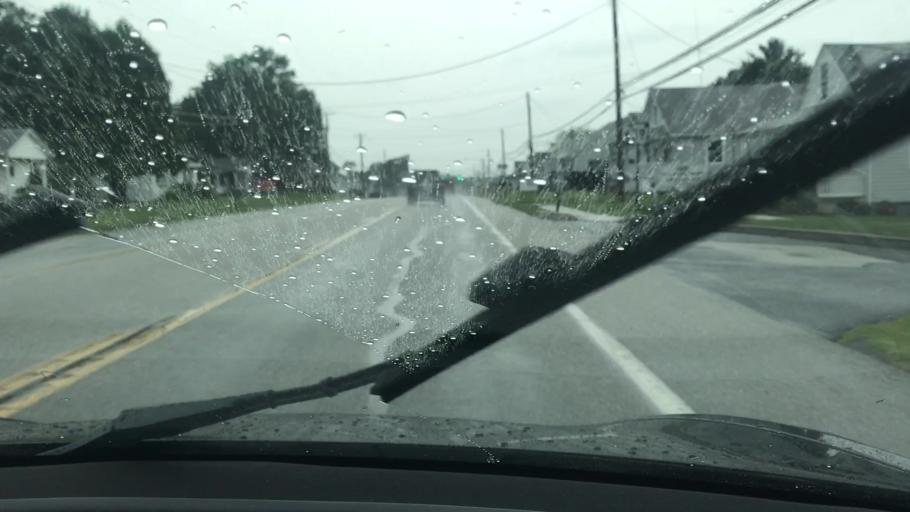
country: US
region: Pennsylvania
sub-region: Dauphin County
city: Lawrence Park
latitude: 40.3368
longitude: -76.8176
